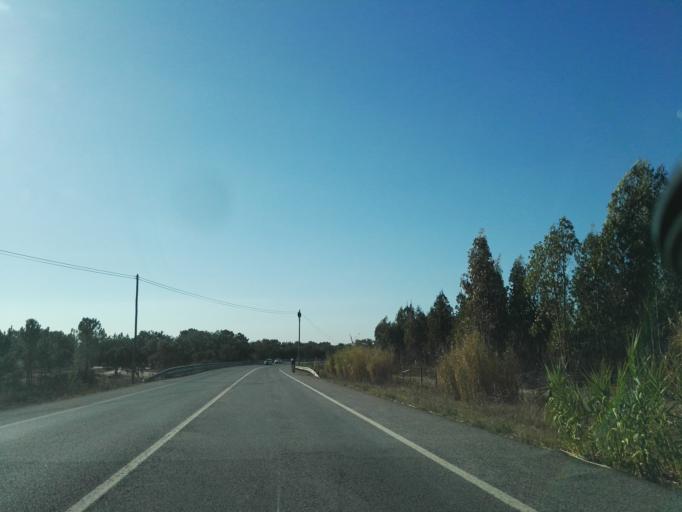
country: PT
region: Santarem
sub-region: Benavente
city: Poceirao
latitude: 38.8463
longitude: -8.7660
